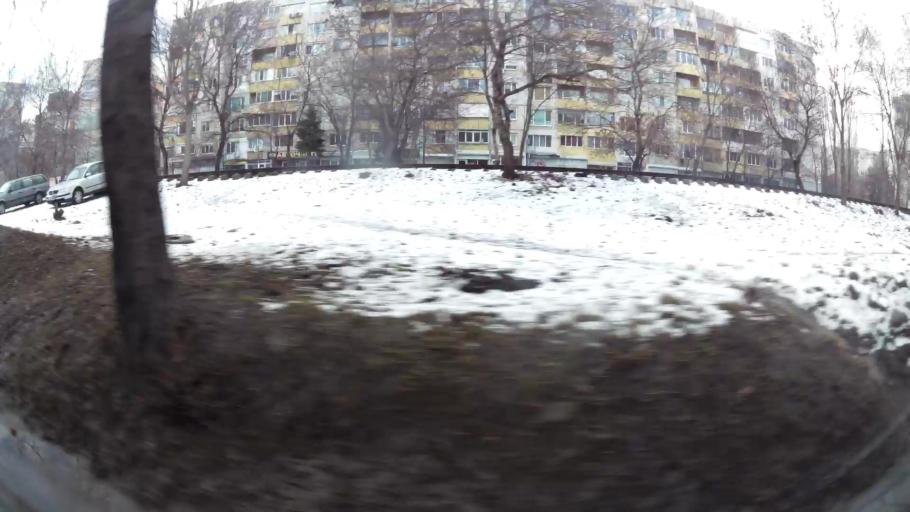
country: BG
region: Sofia-Capital
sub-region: Stolichna Obshtina
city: Sofia
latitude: 42.6991
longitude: 23.2862
